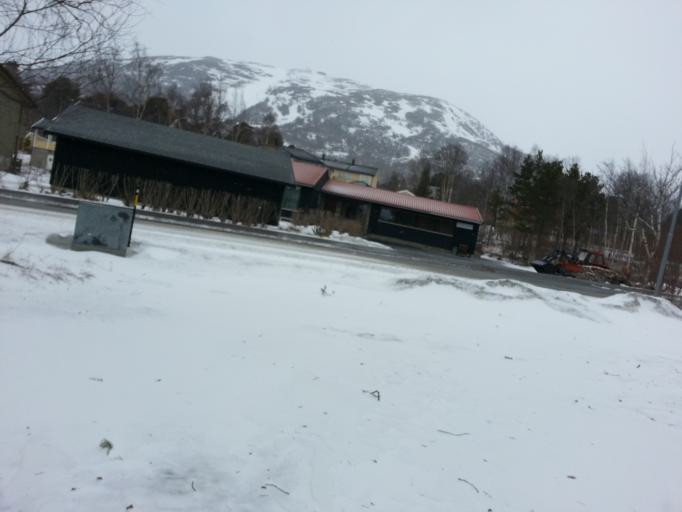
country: NO
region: Sor-Trondelag
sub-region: Oppdal
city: Oppdal
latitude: 62.5956
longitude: 9.6955
